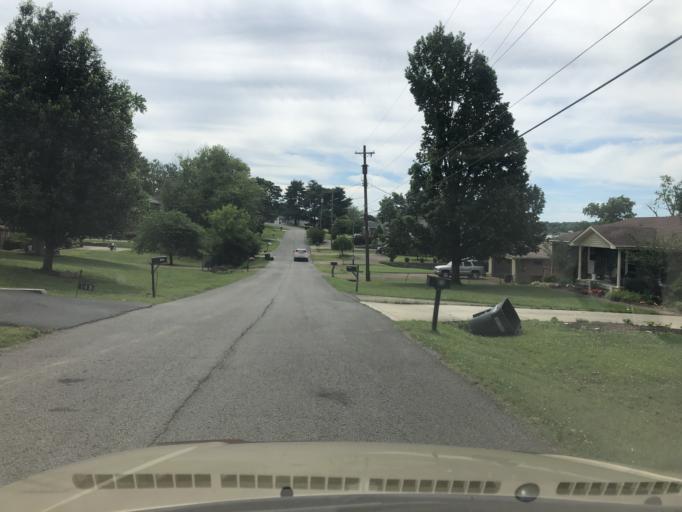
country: US
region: Tennessee
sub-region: Davidson County
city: Lakewood
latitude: 36.2553
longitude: -86.6263
